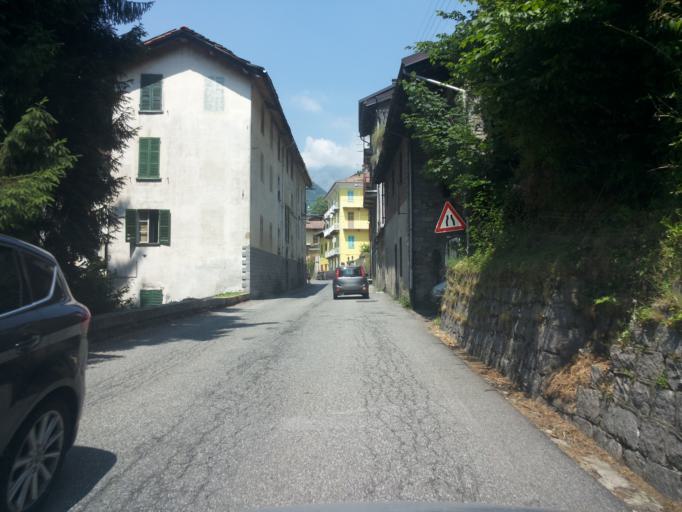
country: IT
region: Piedmont
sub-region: Provincia di Biella
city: Campiglia Cervo
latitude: 45.6626
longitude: 8.0013
